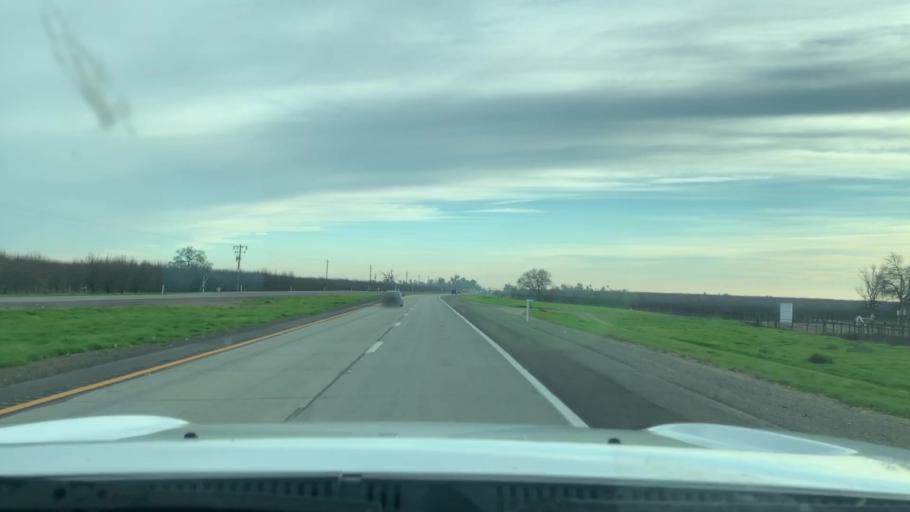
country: US
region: California
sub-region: Kings County
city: Lemoore
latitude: 36.3541
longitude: -119.8086
